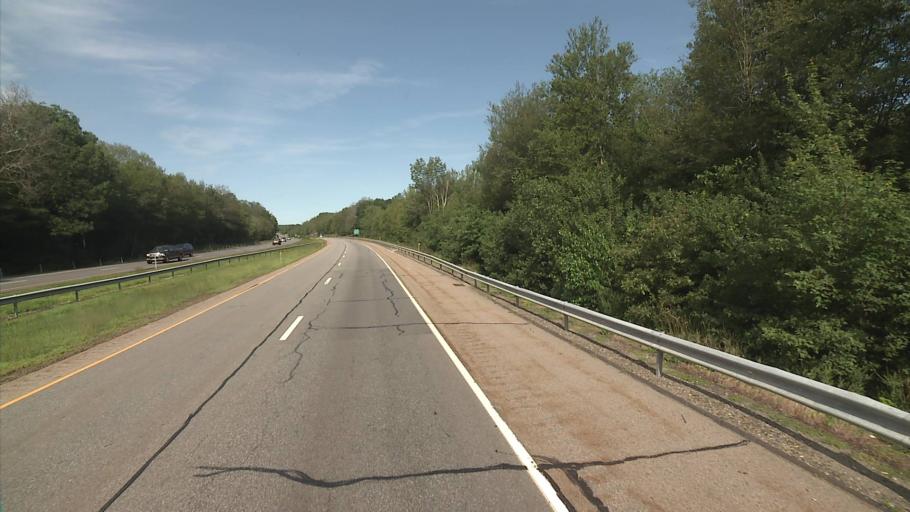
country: US
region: Connecticut
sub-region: New London County
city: Montville Center
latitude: 41.5719
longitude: -72.1914
